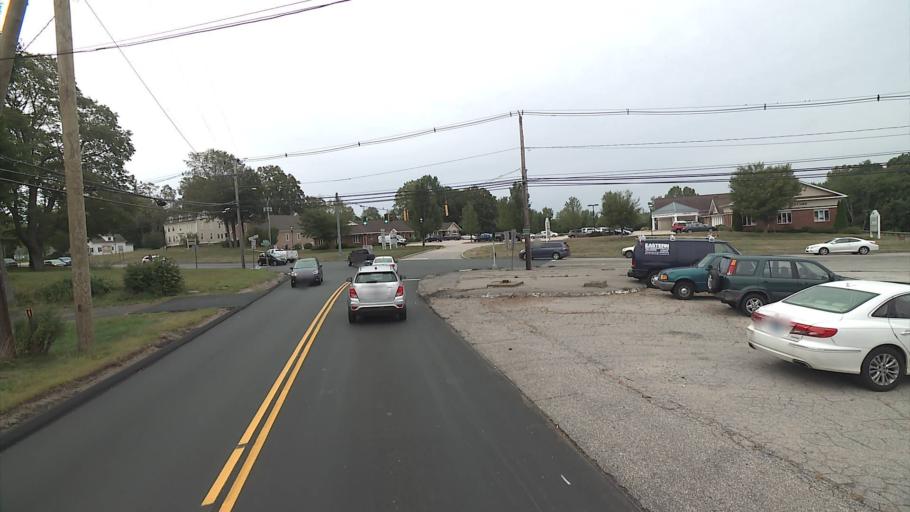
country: US
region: Connecticut
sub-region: New London County
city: Colchester
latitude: 41.5788
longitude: -72.3365
